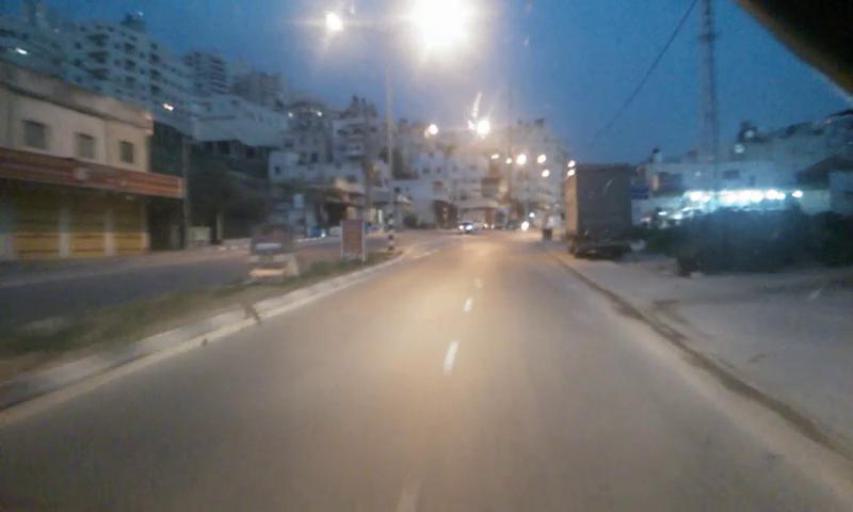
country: PS
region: West Bank
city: Zawata
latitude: 32.2398
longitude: 35.2316
